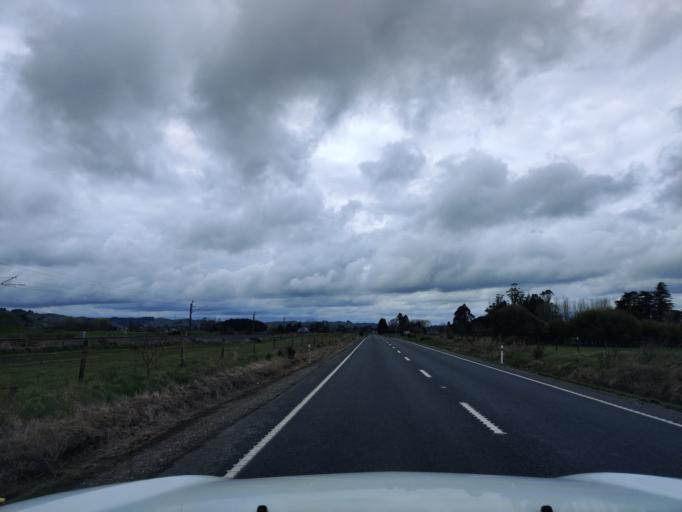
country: NZ
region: Waikato
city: Turangi
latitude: -39.0202
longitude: 175.3794
